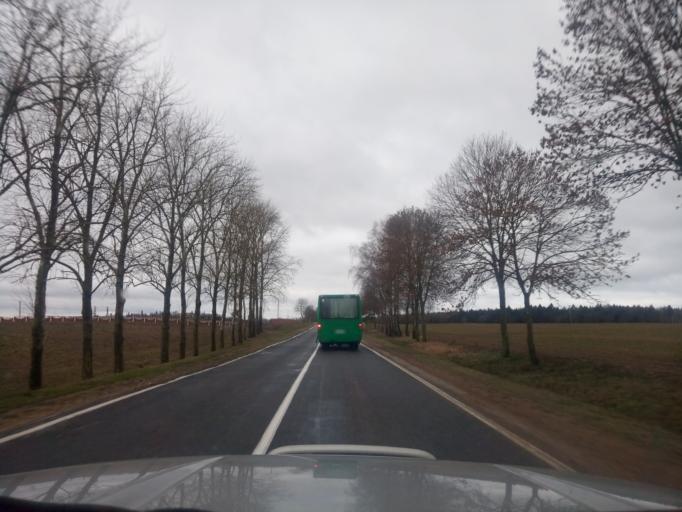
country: BY
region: Minsk
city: Kapyl'
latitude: 53.1718
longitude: 27.1558
